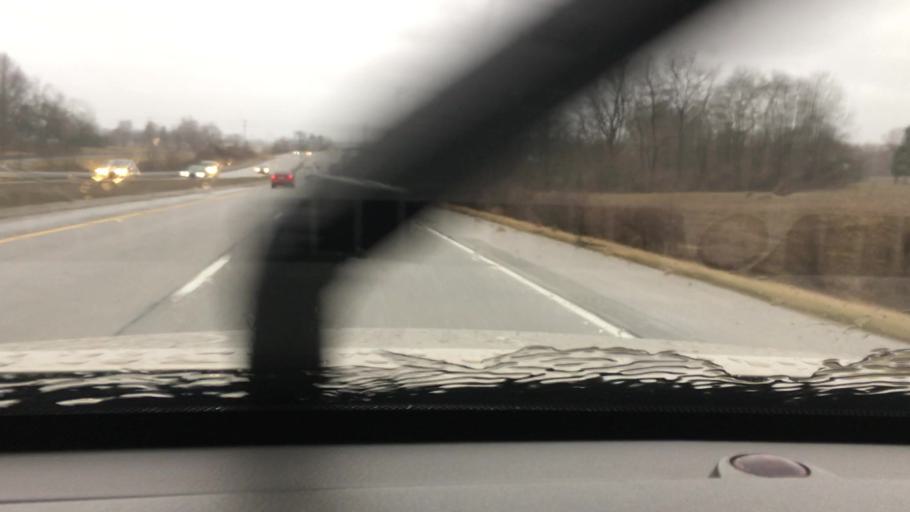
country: US
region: Indiana
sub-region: Delaware County
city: Yorktown
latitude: 40.2193
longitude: -85.5340
